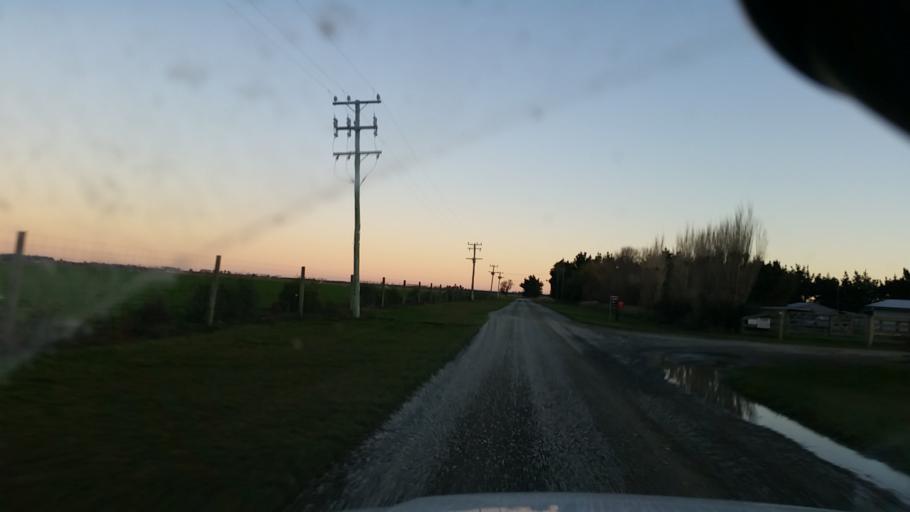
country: NZ
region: Canterbury
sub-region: Ashburton District
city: Tinwald
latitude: -44.0573
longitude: 171.6617
